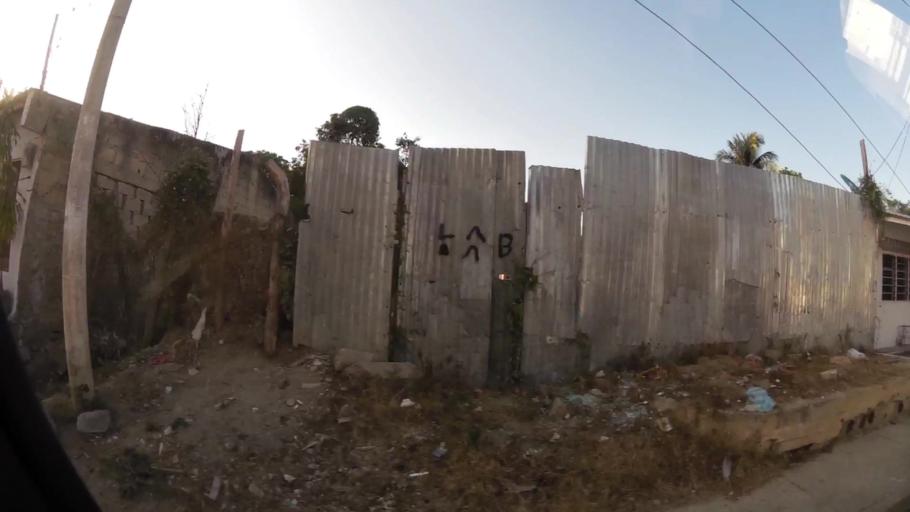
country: CO
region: Bolivar
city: Cartagena
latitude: 10.3988
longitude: -75.4783
